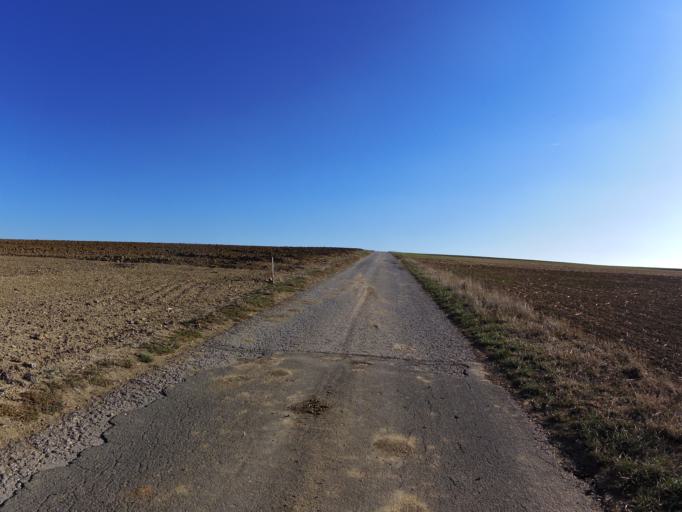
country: DE
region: Bavaria
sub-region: Regierungsbezirk Unterfranken
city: Eibelstadt
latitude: 49.7055
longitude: 9.9776
